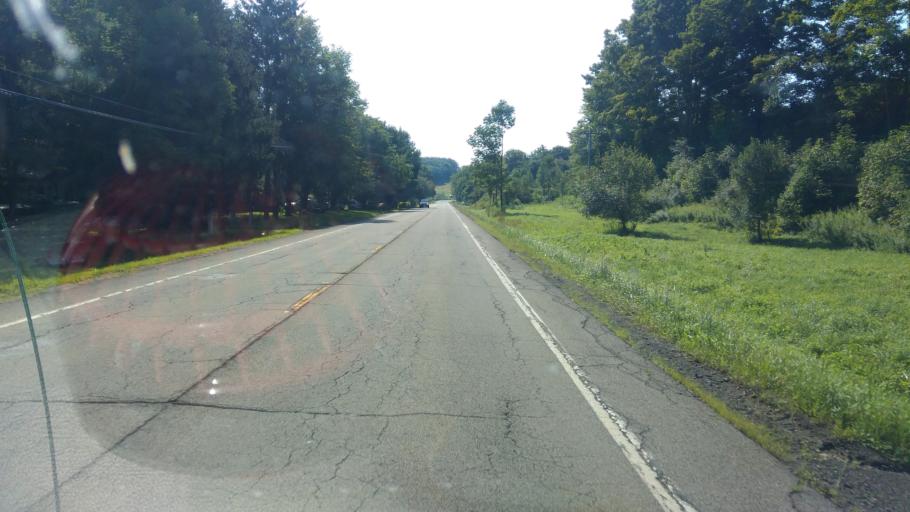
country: US
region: New York
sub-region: Allegany County
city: Cuba
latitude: 42.1870
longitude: -78.2619
